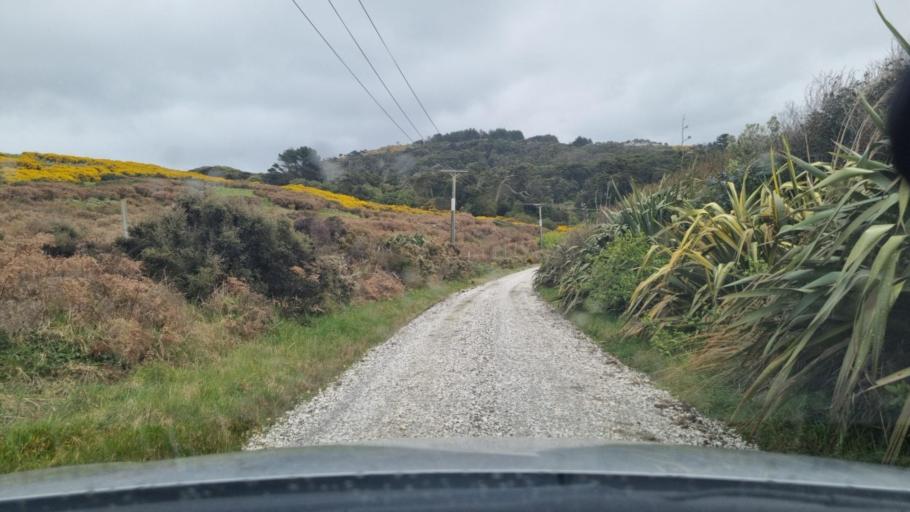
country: NZ
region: Southland
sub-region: Invercargill City
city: Bluff
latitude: -46.5880
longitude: 168.3039
